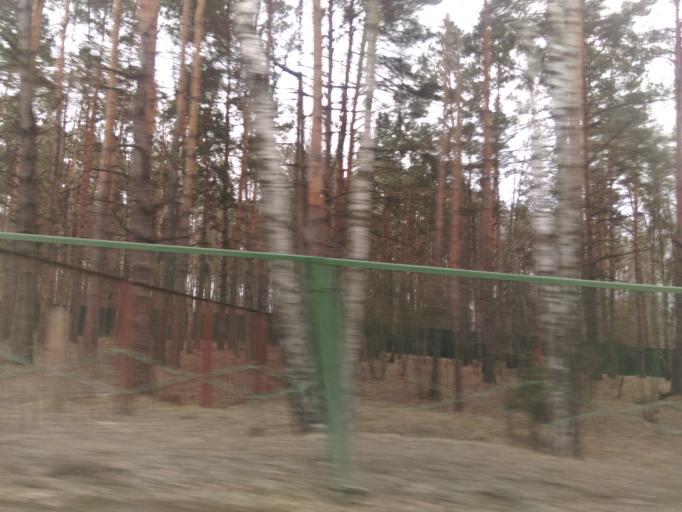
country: RU
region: Moskovskaya
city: Gorki Vtoryye
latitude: 55.7188
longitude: 37.1279
